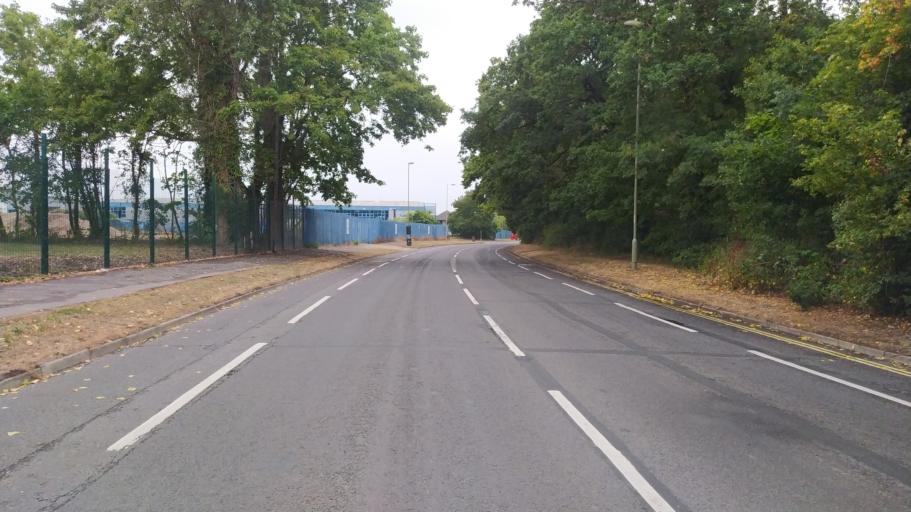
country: GB
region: England
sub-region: Hampshire
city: Havant
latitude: 50.8635
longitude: -0.9695
